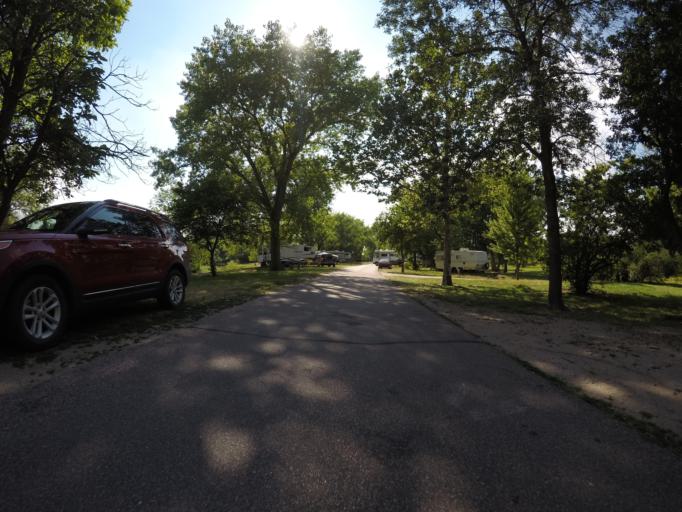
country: US
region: Nebraska
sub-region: Buffalo County
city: Kearney
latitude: 40.6541
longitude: -98.9980
